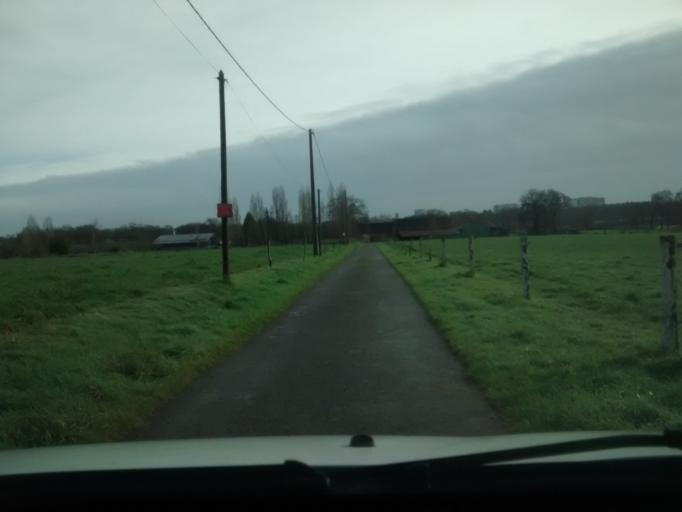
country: FR
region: Brittany
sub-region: Departement d'Ille-et-Vilaine
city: Vezin-le-Coquet
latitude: 48.1296
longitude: -1.7322
